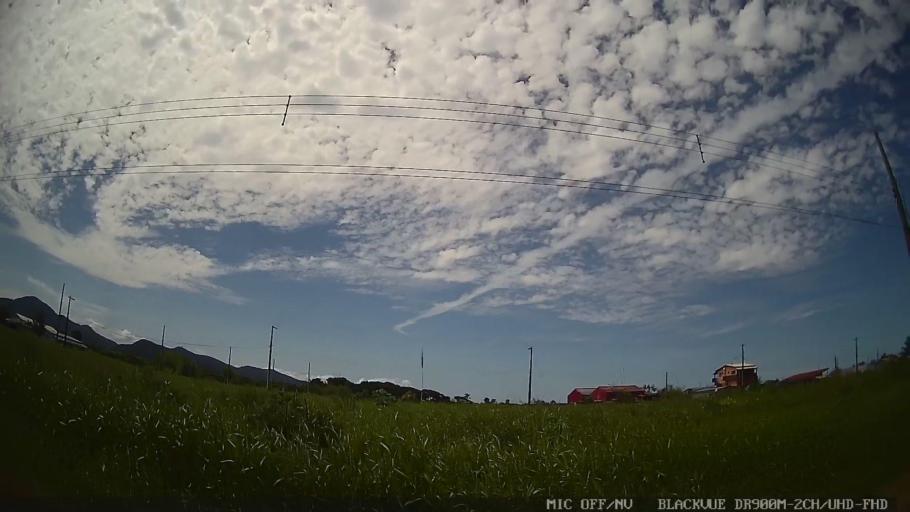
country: BR
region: Sao Paulo
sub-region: Iguape
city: Iguape
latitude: -24.7251
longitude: -47.5201
